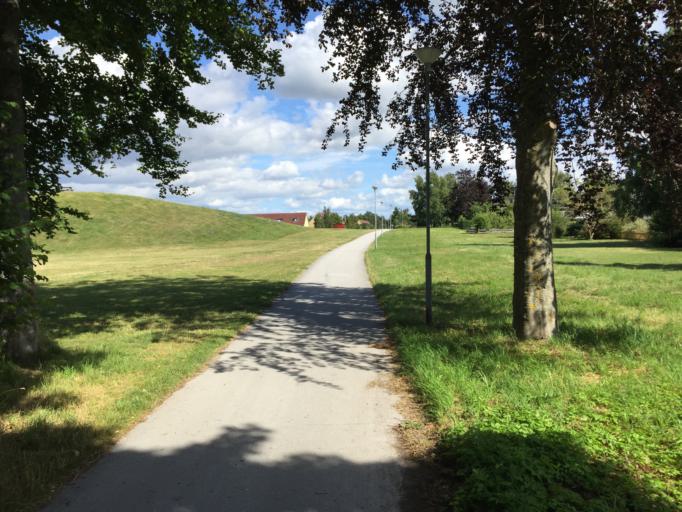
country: SE
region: Gotland
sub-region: Gotland
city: Visby
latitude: 57.6136
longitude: 18.2961
